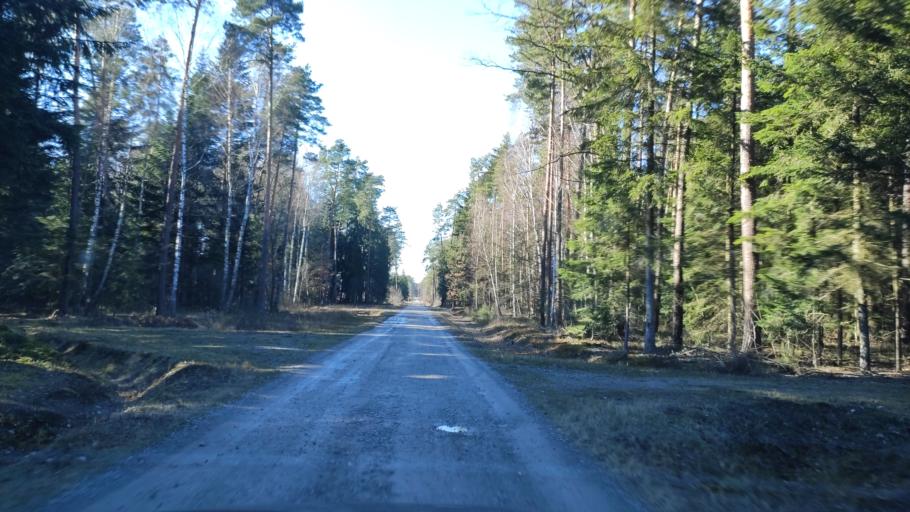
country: PL
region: Masovian Voivodeship
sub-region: Powiat radomski
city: Jedlnia-Letnisko
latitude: 51.4687
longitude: 21.3088
